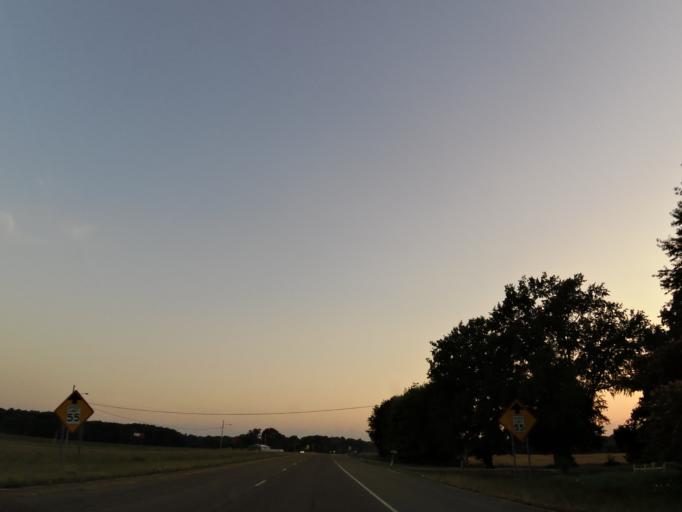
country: US
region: Tennessee
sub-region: Carroll County
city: McKenzie
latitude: 36.1498
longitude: -88.4740
